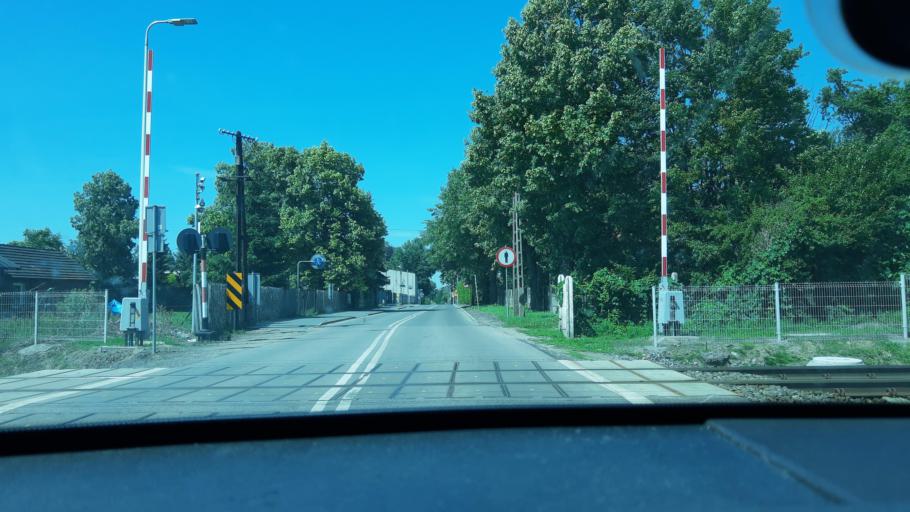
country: PL
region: Lodz Voivodeship
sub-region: Powiat zdunskowolski
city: Zdunska Wola
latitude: 51.6108
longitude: 18.9383
